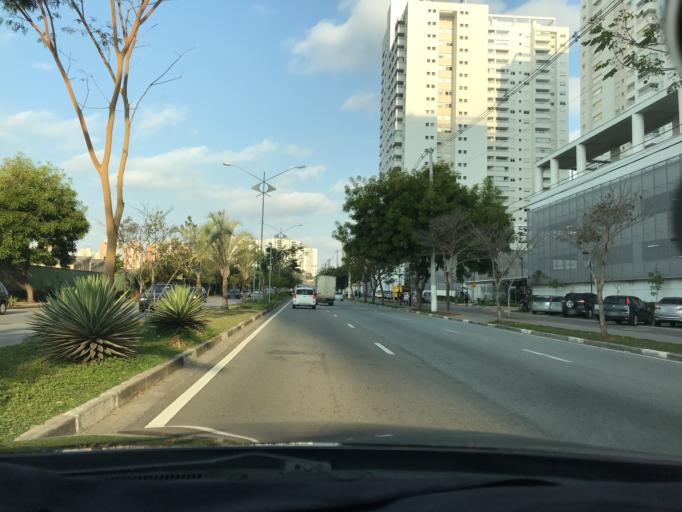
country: BR
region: Sao Paulo
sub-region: Osasco
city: Osasco
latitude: -23.5340
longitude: -46.7697
